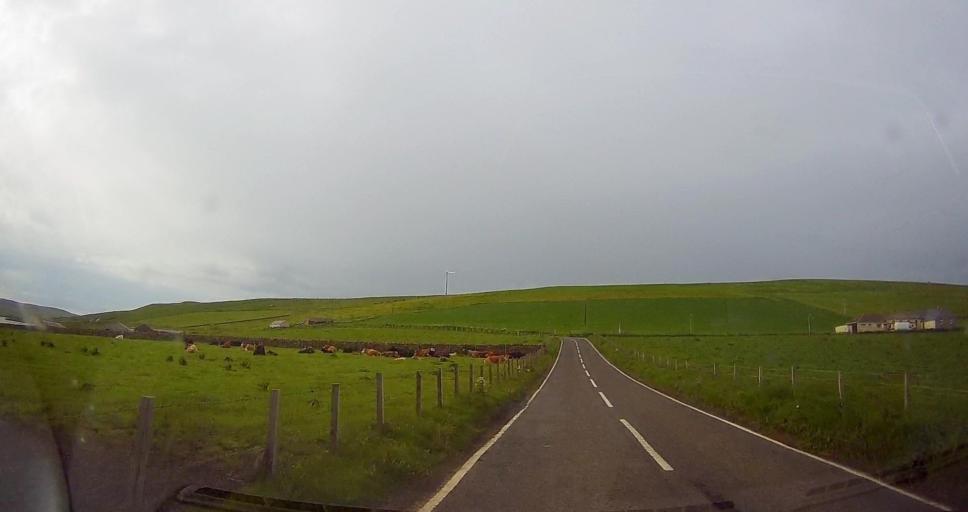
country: GB
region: Scotland
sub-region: Orkney Islands
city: Stromness
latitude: 59.1183
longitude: -3.3050
